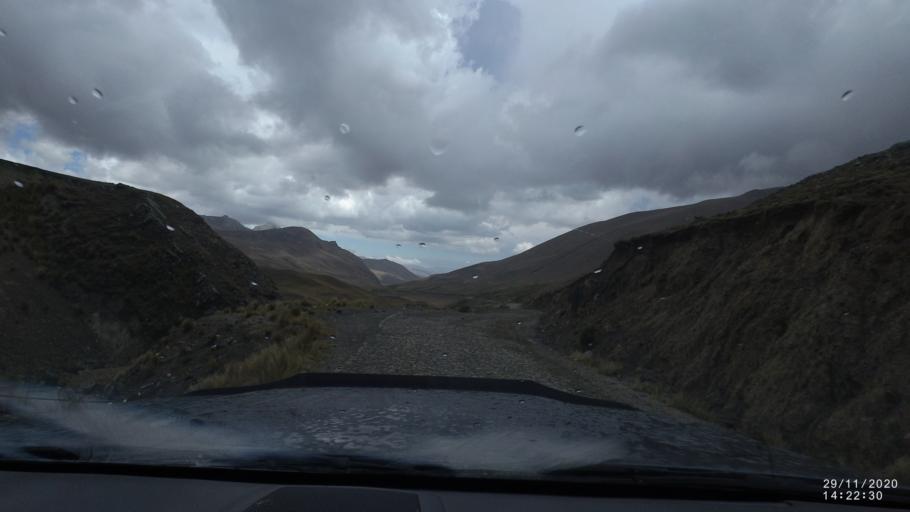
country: BO
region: Cochabamba
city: Sipe Sipe
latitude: -17.2529
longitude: -66.3885
